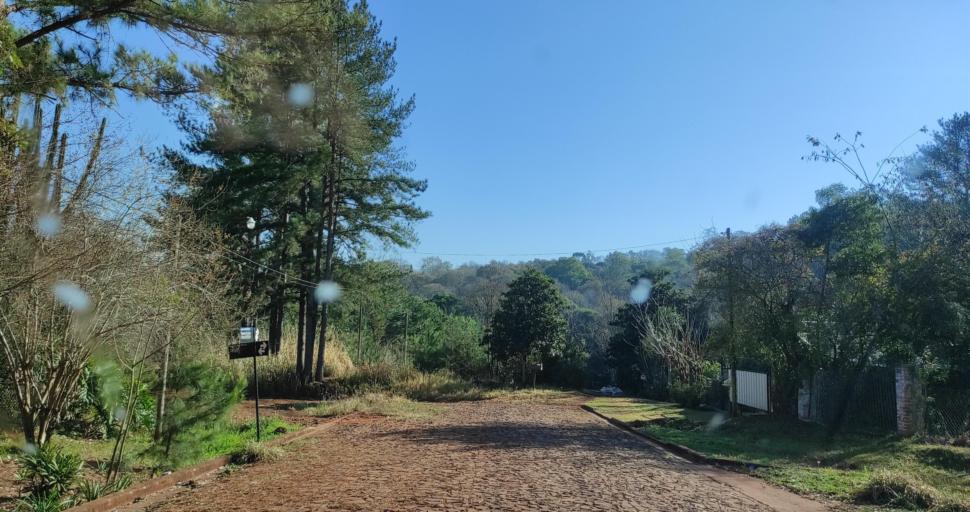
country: AR
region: Misiones
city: Capiovi
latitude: -26.8630
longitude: -55.0437
